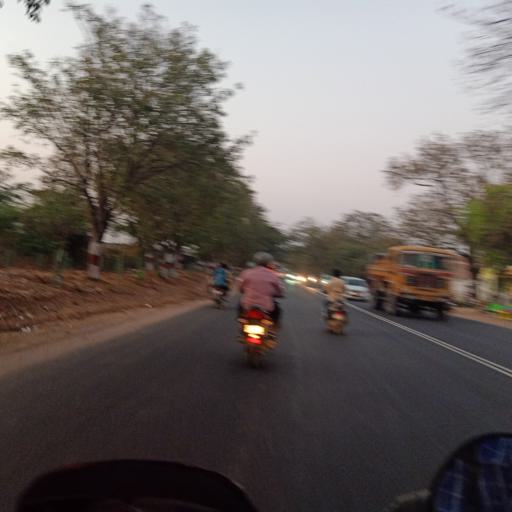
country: IN
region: Telangana
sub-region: Rangareddi
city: Secunderabad
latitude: 17.5481
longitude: 78.5354
